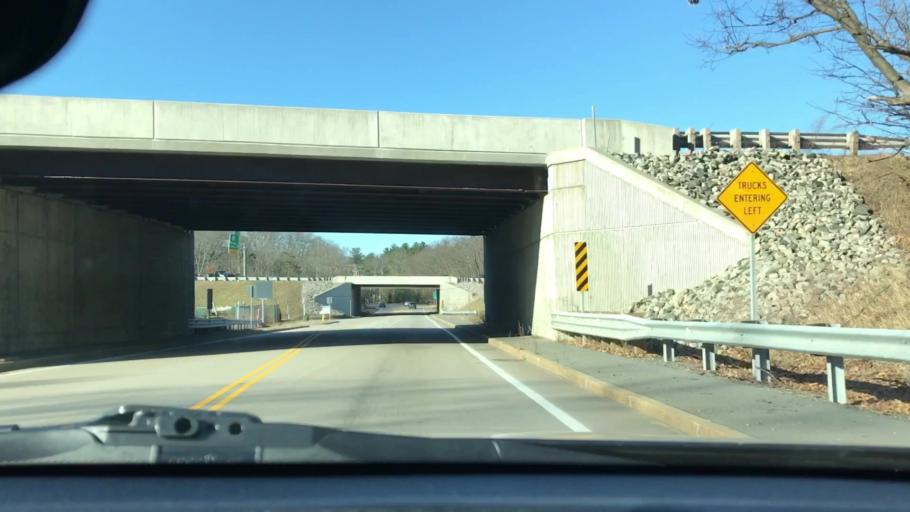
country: US
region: Massachusetts
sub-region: Norfolk County
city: Needham
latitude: 42.2640
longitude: -71.2051
